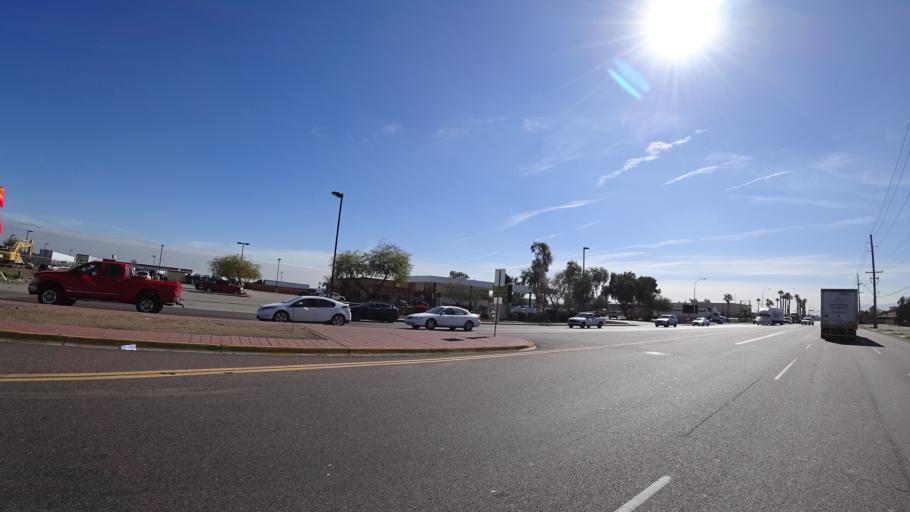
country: US
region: Arizona
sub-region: Maricopa County
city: Tolleson
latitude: 33.4617
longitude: -112.1866
